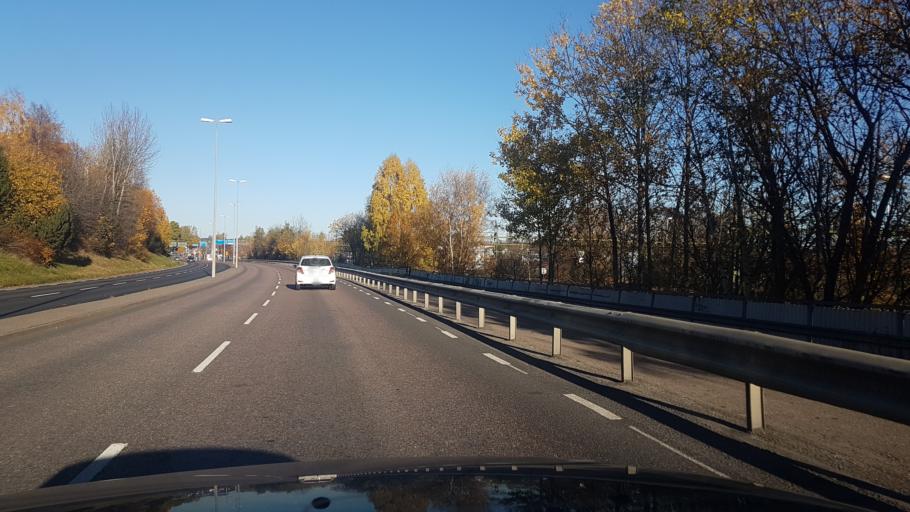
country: SE
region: Stockholm
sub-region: Sigtuna Kommun
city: Marsta
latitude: 59.6247
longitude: 17.8606
